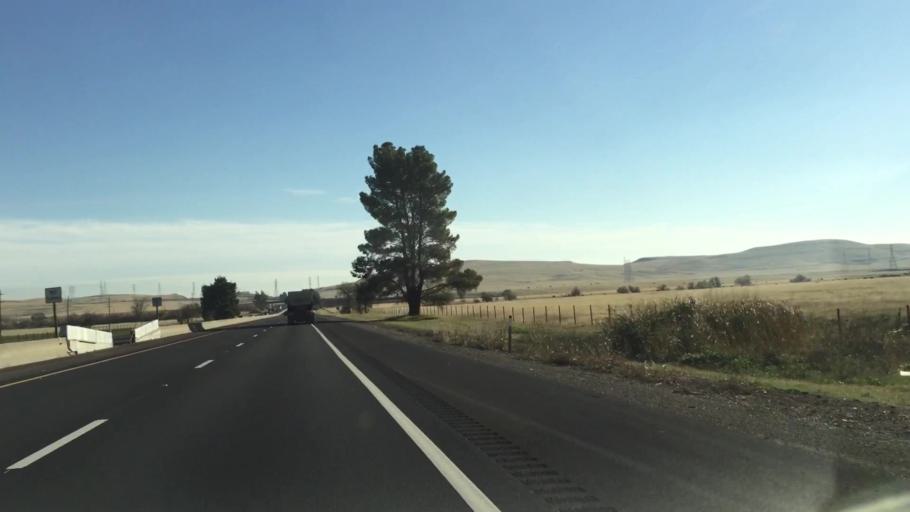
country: US
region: California
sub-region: Butte County
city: Thermalito
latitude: 39.5622
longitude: -121.6062
